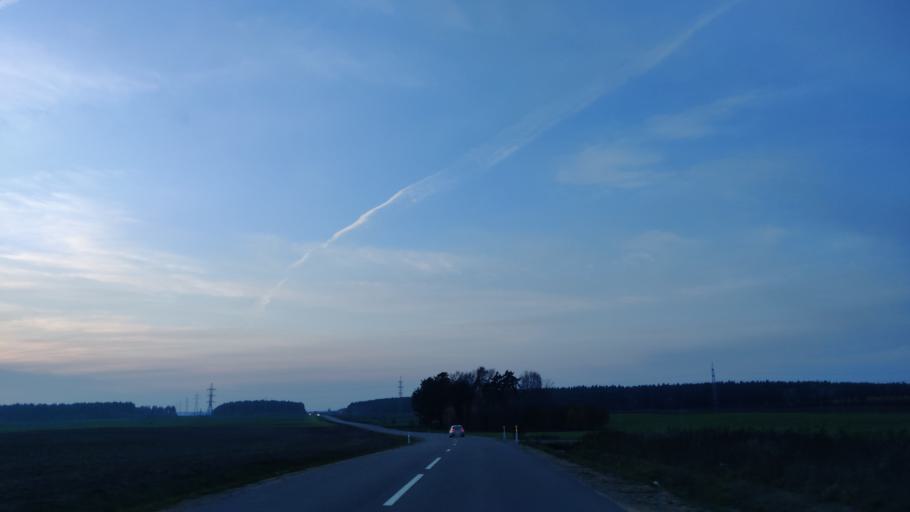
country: LT
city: Lentvaris
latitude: 54.5924
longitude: 25.0463
